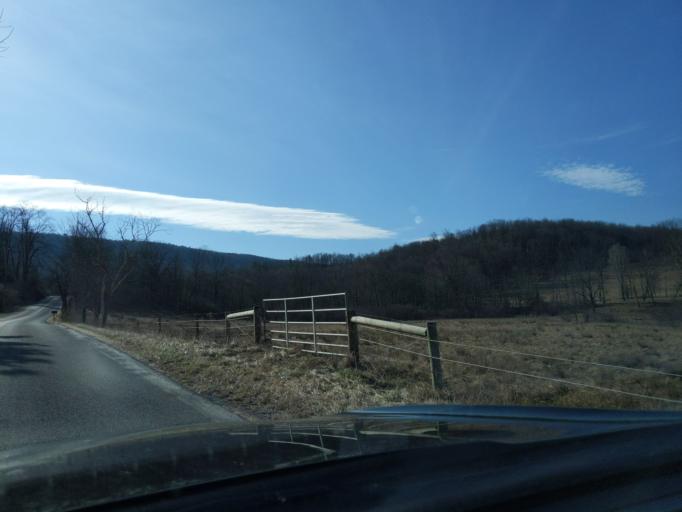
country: US
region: Pennsylvania
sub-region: Blair County
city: Hollidaysburg
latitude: 40.4066
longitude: -78.3211
